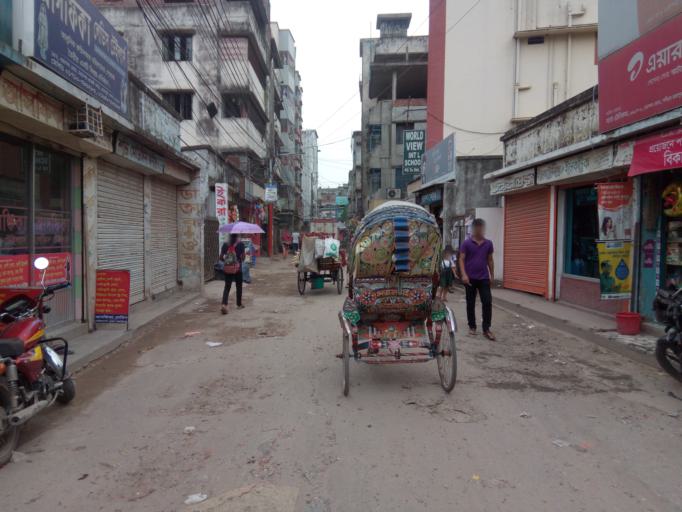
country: BD
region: Dhaka
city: Paltan
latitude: 23.7633
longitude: 90.4159
